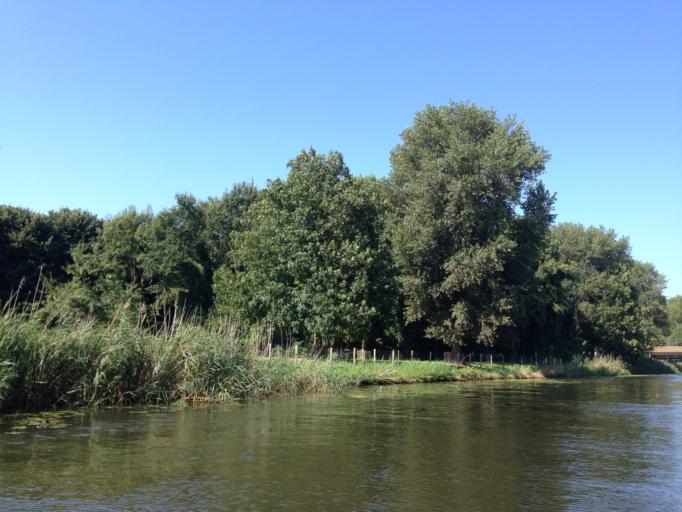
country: NL
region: Flevoland
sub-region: Gemeente Almere
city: Almere Stad
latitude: 52.3715
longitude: 5.2077
